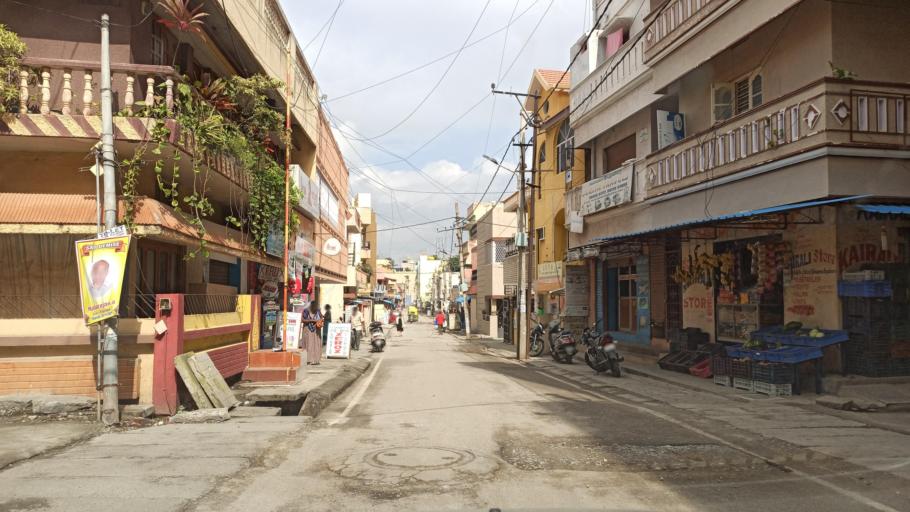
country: IN
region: Karnataka
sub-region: Bangalore Urban
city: Bangalore
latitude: 13.0056
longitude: 77.6747
